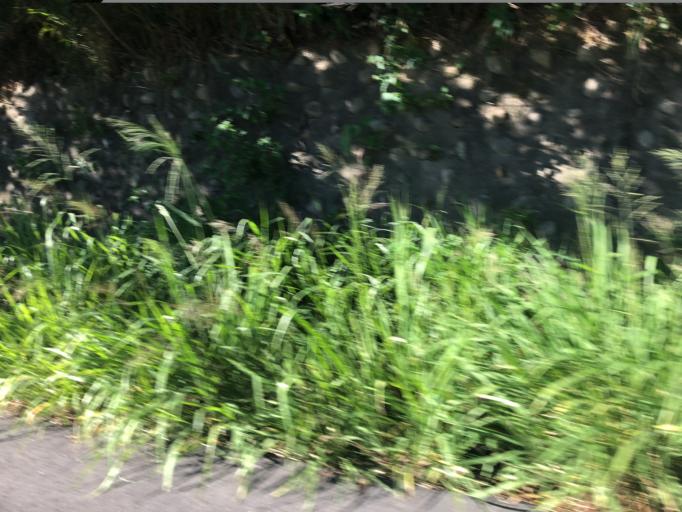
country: TW
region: Taiwan
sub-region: Hsinchu
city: Hsinchu
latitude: 24.7514
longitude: 120.9804
